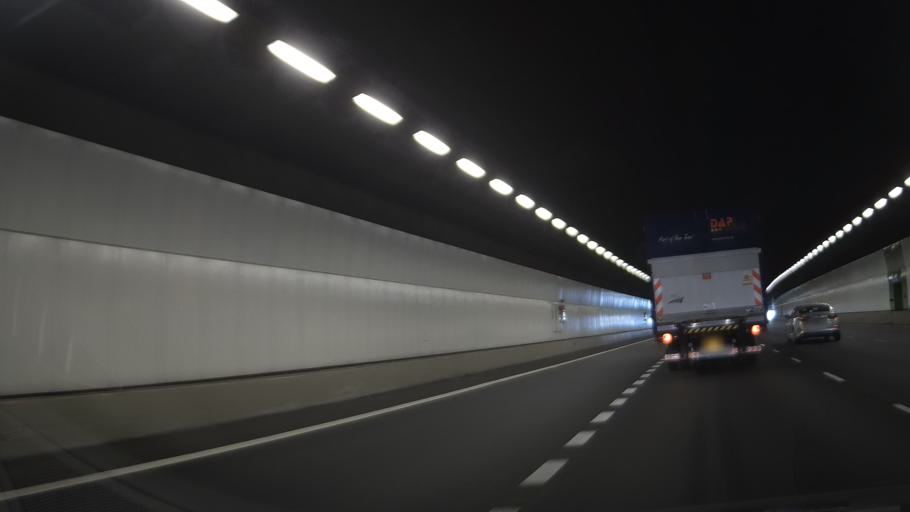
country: SG
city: Singapore
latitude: 1.3252
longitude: 103.8701
